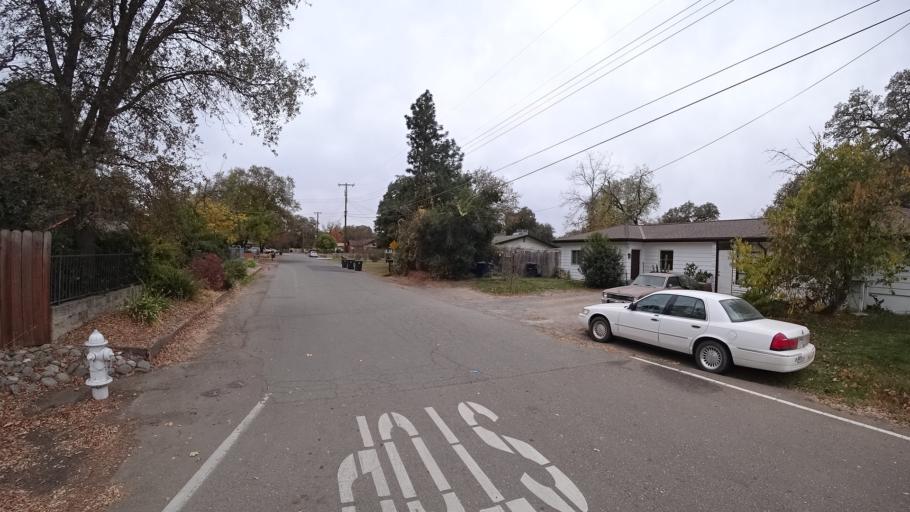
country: US
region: California
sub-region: Sacramento County
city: Citrus Heights
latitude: 38.7072
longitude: -121.2944
